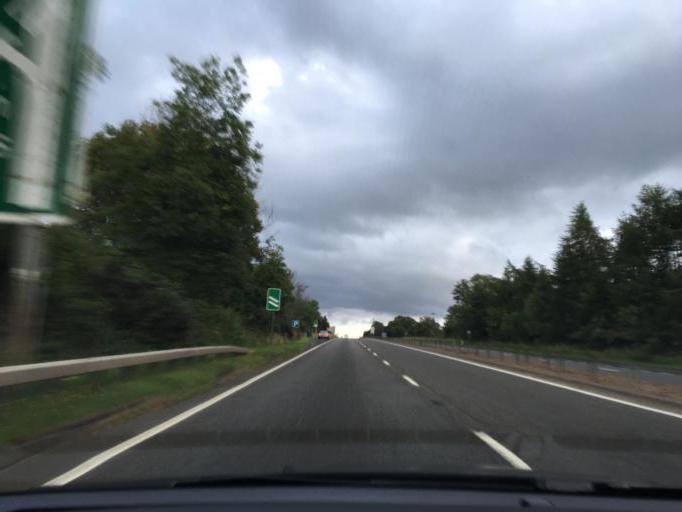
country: GB
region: Scotland
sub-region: Highland
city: Inverness
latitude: 57.4550
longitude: -4.1630
